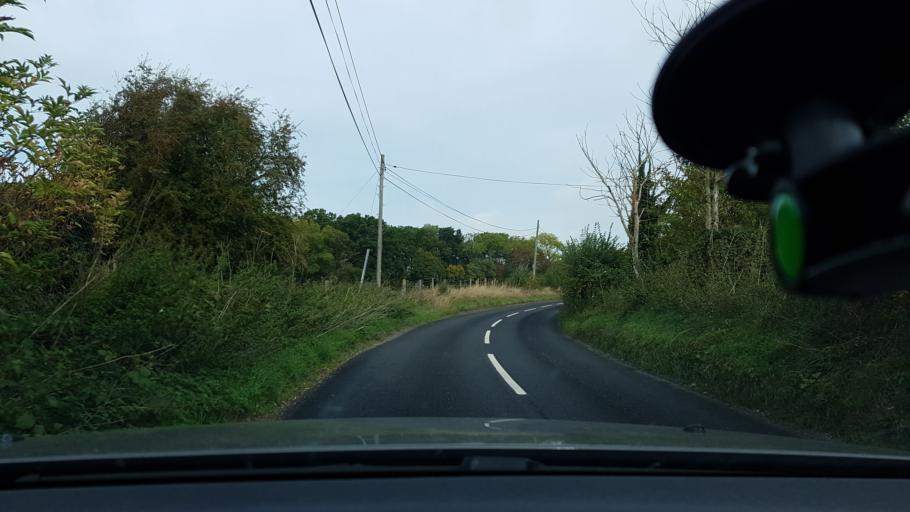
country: GB
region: England
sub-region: West Berkshire
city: Kintbury
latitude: 51.3908
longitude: -1.4315
